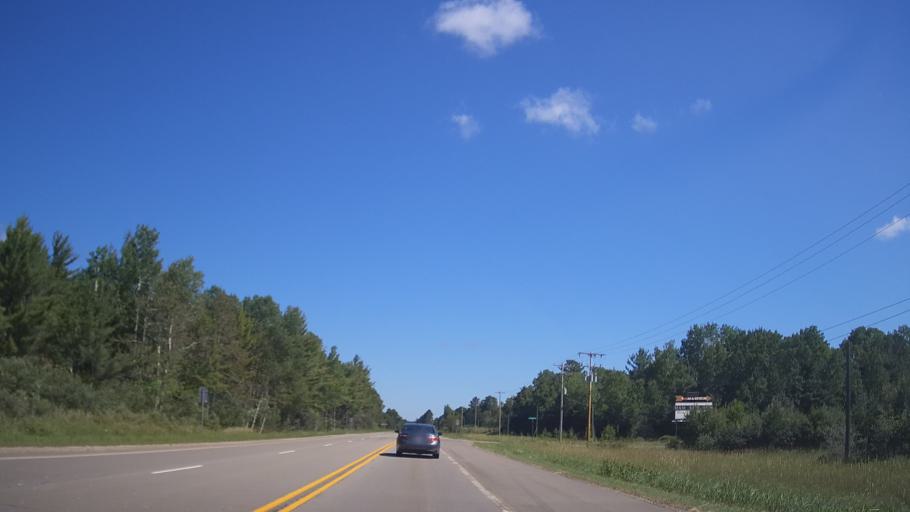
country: US
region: Michigan
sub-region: Cheboygan County
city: Indian River
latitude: 45.5279
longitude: -84.7819
